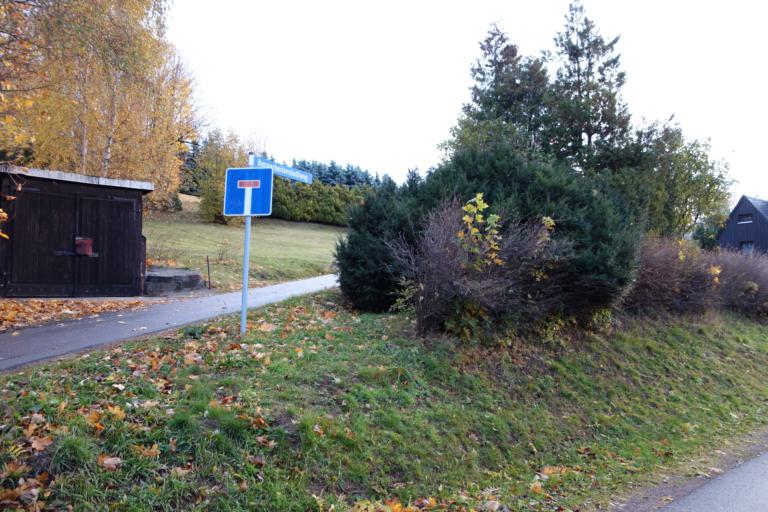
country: DE
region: Saxony
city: Altenberg
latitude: 50.7636
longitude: 13.7684
